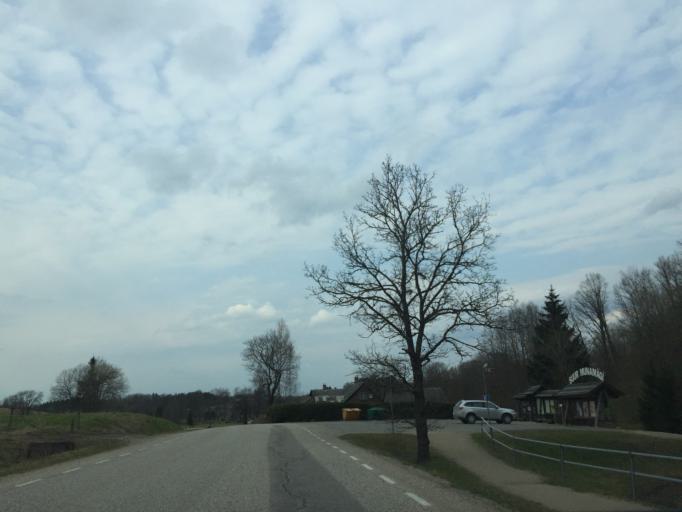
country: EE
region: Vorumaa
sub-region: Voru linn
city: Voru
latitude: 57.7146
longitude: 27.0552
